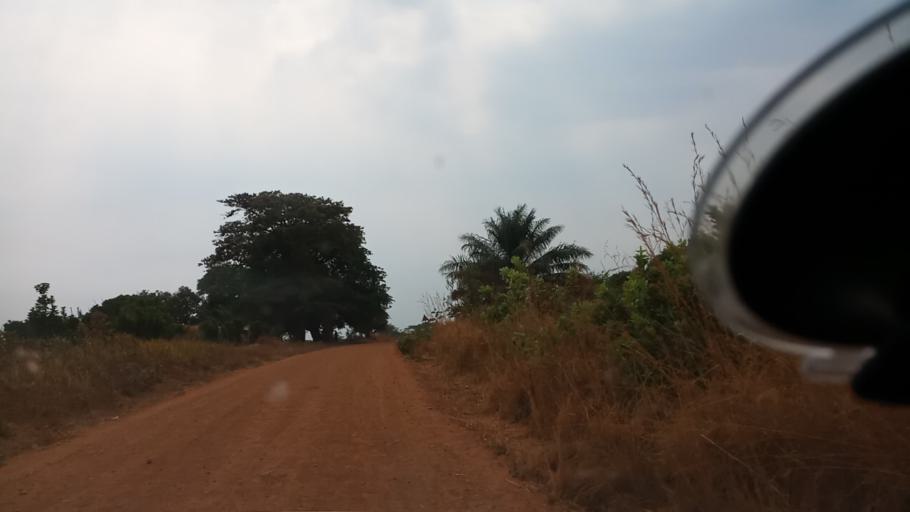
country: ZM
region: Luapula
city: Nchelenge
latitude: -9.0988
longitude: 28.3070
